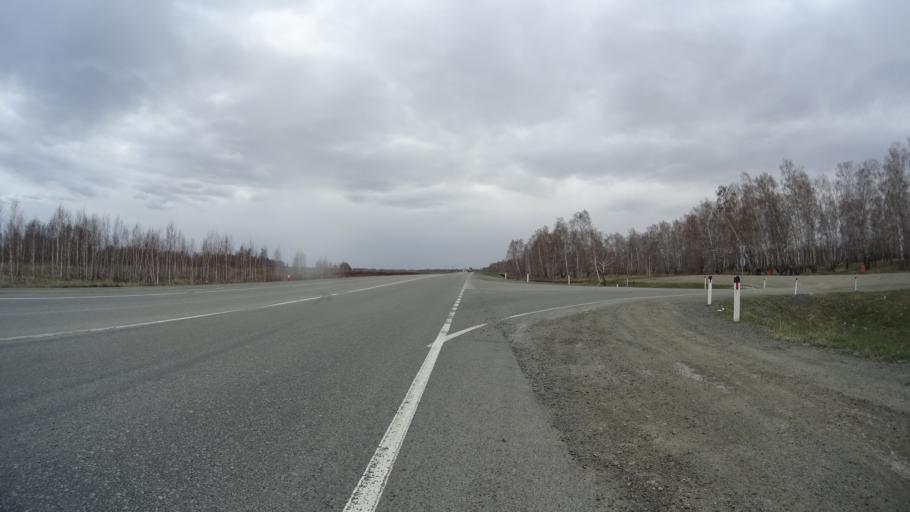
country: RU
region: Chelyabinsk
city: Krasnogorskiy
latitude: 54.6928
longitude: 61.2492
